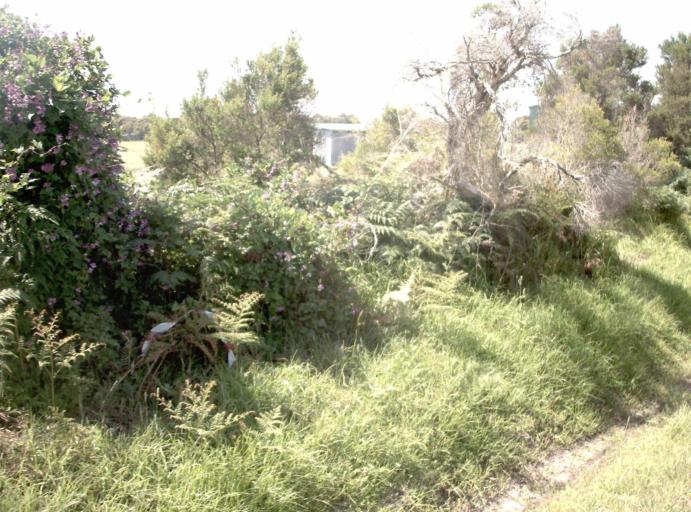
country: AU
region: Victoria
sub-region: Bass Coast
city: North Wonthaggi
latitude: -38.6227
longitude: 145.7222
